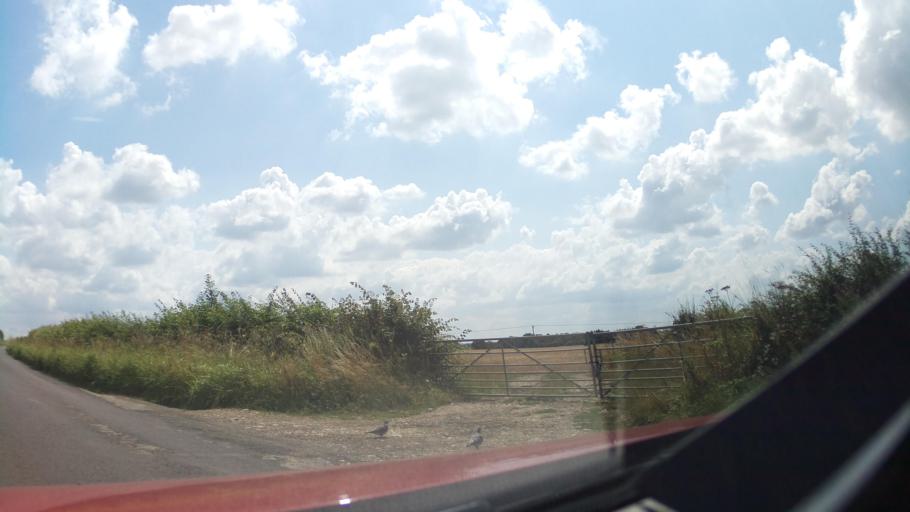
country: GB
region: England
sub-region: Wiltshire
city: Hankerton
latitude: 51.6331
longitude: -2.0576
